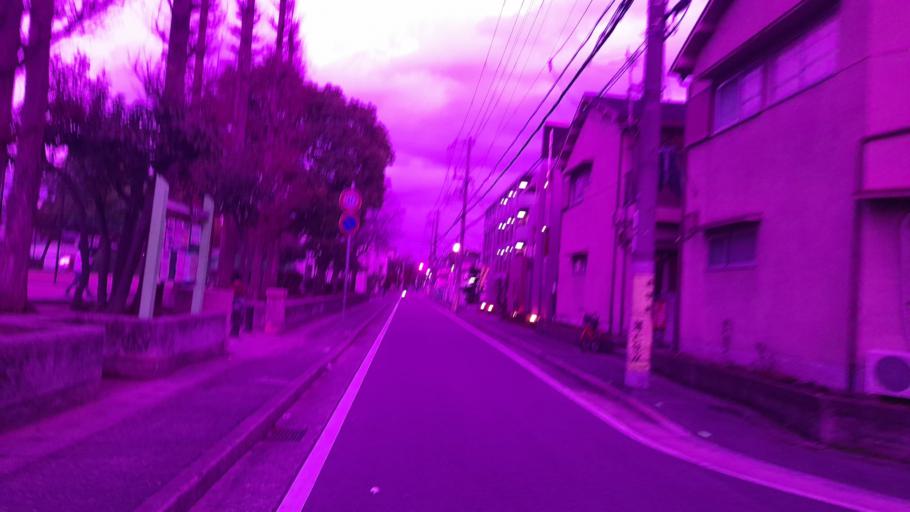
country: JP
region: Hyogo
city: Amagasaki
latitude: 34.7454
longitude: 135.4353
